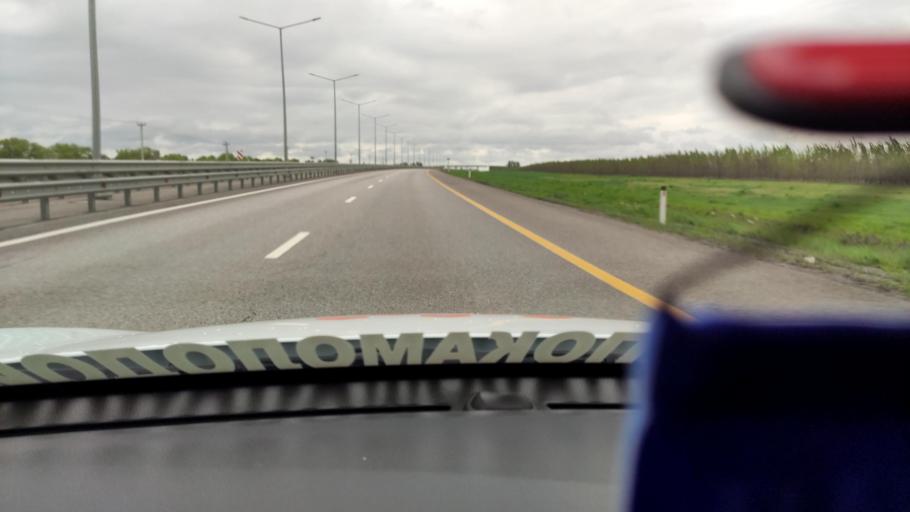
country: RU
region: Voronezj
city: Podkletnoye
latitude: 51.5785
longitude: 39.4644
